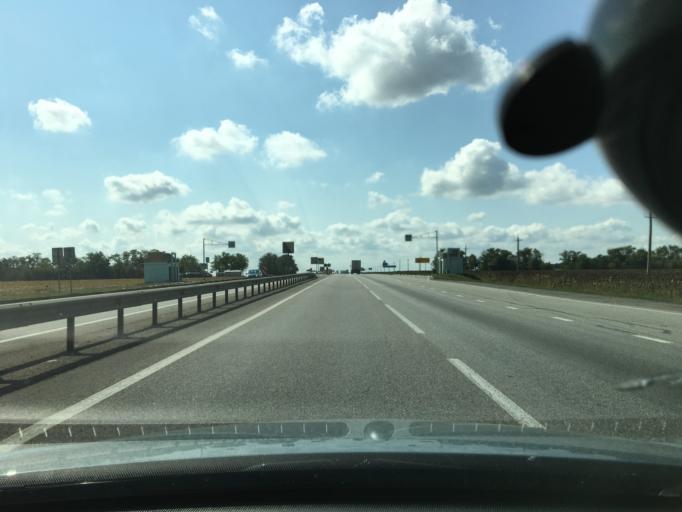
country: RU
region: Krasnodarskiy
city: Krasnoye
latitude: 46.7558
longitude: 39.6604
